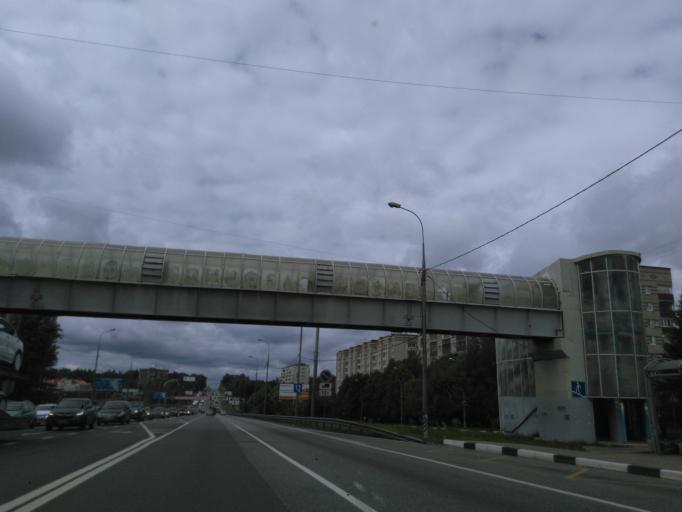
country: RU
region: Moskovskaya
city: Solnechnogorsk
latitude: 56.1954
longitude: 36.9651
